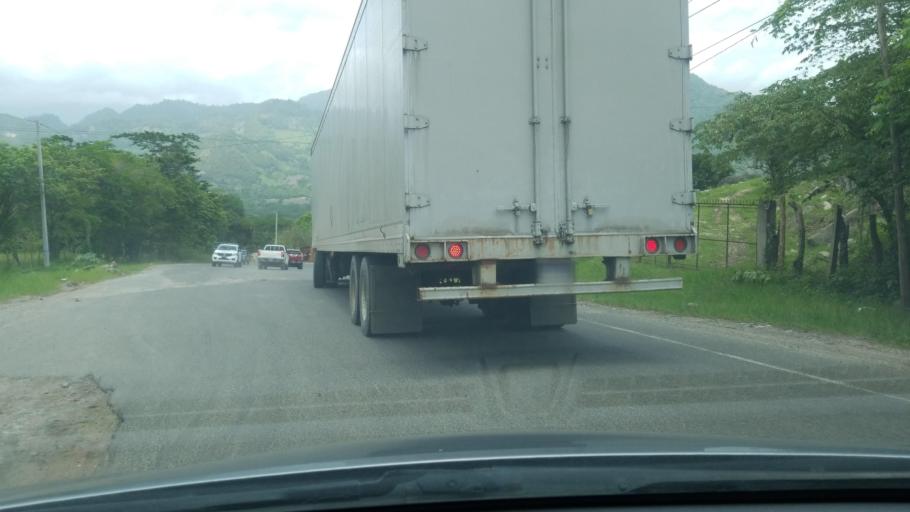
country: HN
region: Copan
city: Santa Rosa de Copan
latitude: 14.7247
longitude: -88.7700
